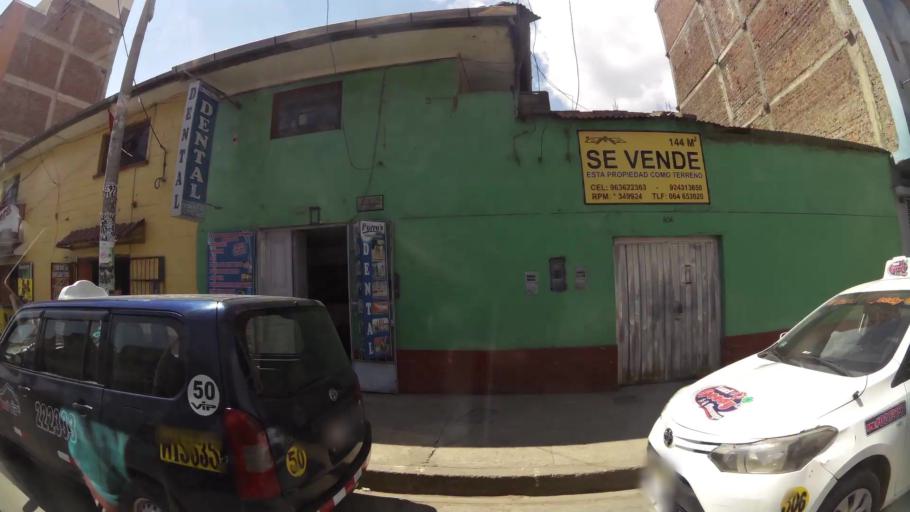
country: PE
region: Junin
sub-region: Provincia de Huancayo
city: El Tambo
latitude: -12.0744
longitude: -75.2122
